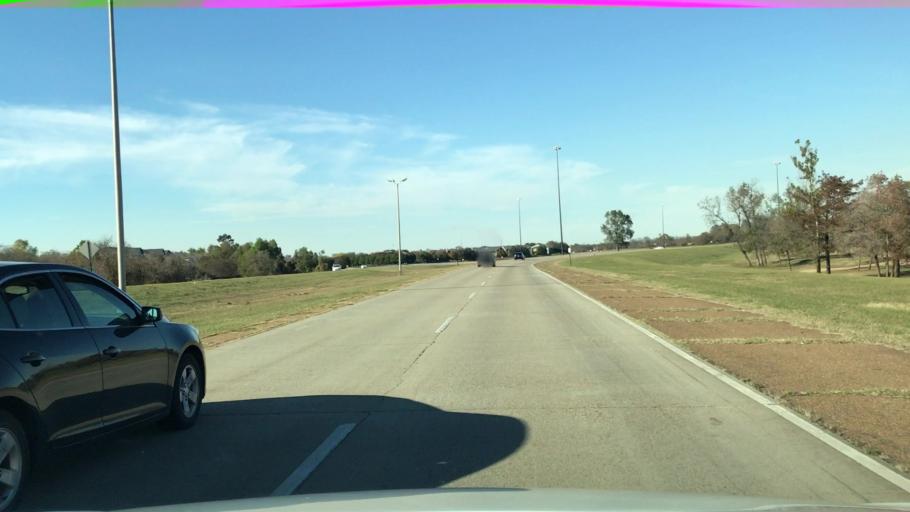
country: US
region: Louisiana
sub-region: Bossier Parish
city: Bossier City
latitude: 32.4649
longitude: -93.6845
